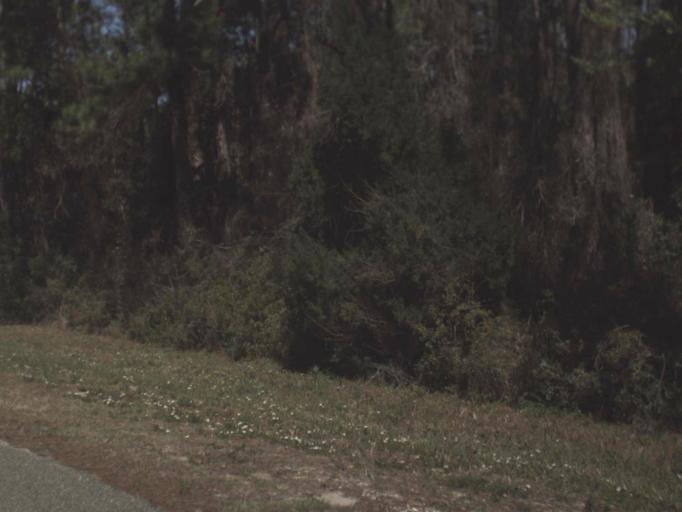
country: US
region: Florida
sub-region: Gulf County
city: Port Saint Joe
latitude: 29.7532
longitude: -85.2493
